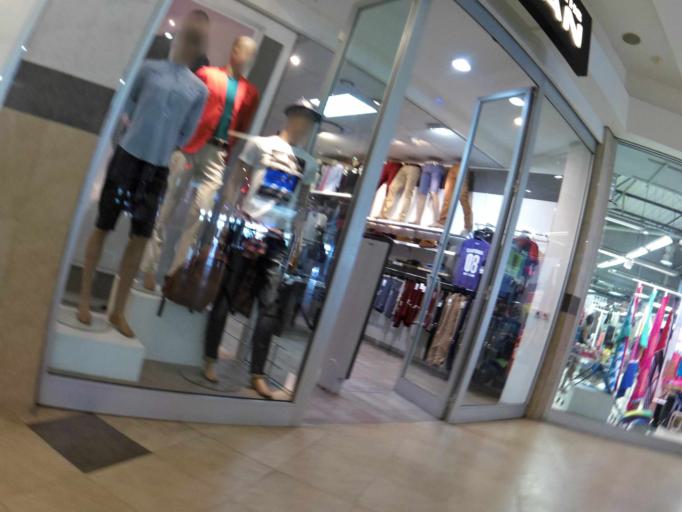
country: GH
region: Greater Accra
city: Medina Estates
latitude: 5.6231
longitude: -0.1735
